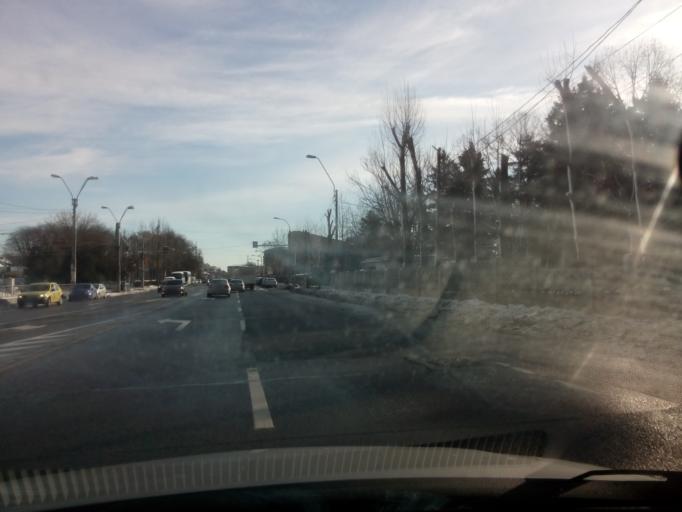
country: RO
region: Ilfov
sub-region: Comuna Popesti-Leordeni
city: Popesti-Leordeni
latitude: 44.3835
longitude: 26.1458
